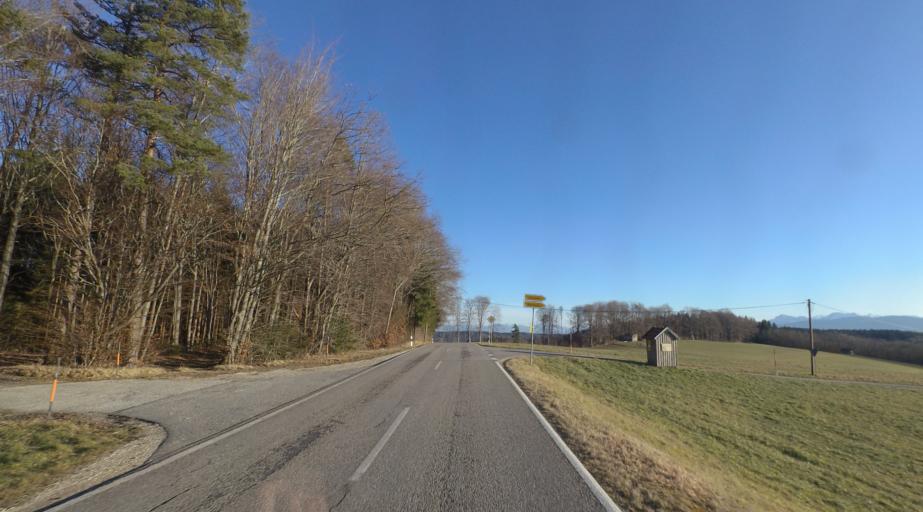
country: DE
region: Bavaria
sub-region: Upper Bavaria
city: Taching am See
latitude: 47.9969
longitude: 12.7053
